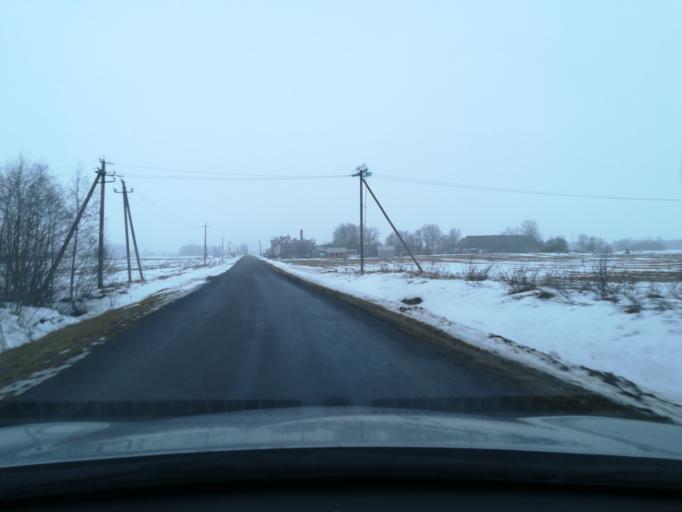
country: EE
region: Harju
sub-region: Raasiku vald
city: Raasiku
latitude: 59.3549
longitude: 25.2065
